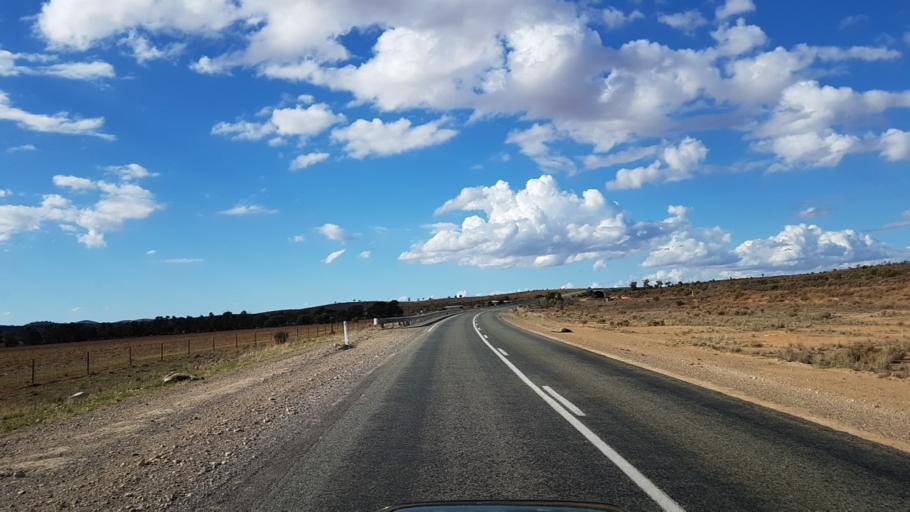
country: AU
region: South Australia
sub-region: Peterborough
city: Peterborough
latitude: -32.9563
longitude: 138.8967
